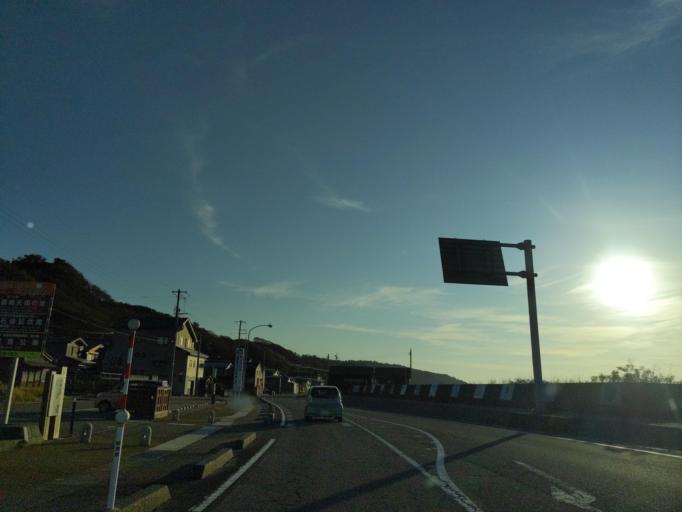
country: JP
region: Niigata
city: Nagaoka
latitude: 37.5436
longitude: 138.6868
